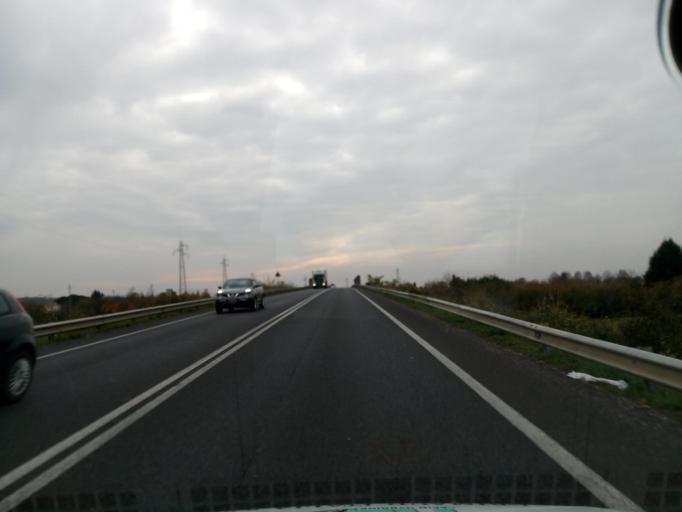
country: IT
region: Veneto
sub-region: Provincia di Treviso
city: Crocetta-Nogare
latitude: 45.8282
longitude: 12.0182
